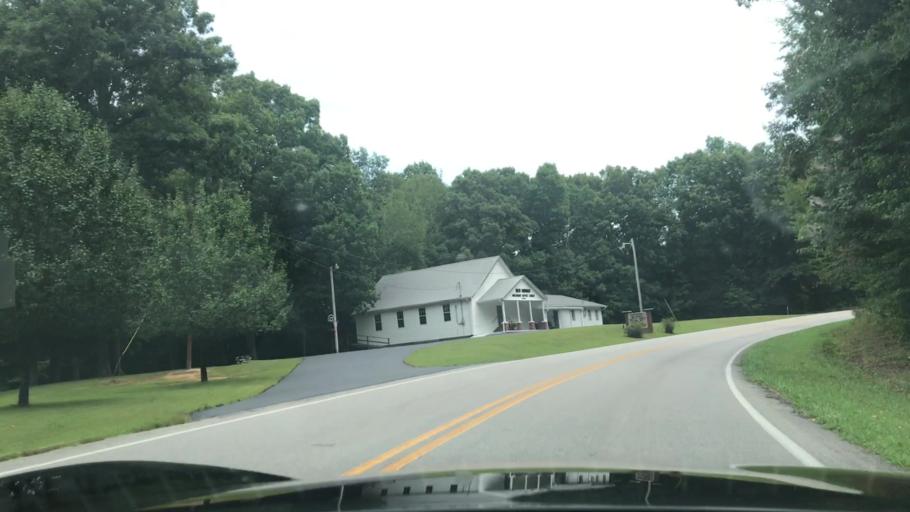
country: US
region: Kentucky
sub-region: Butler County
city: Morgantown
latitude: 37.1847
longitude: -86.8741
